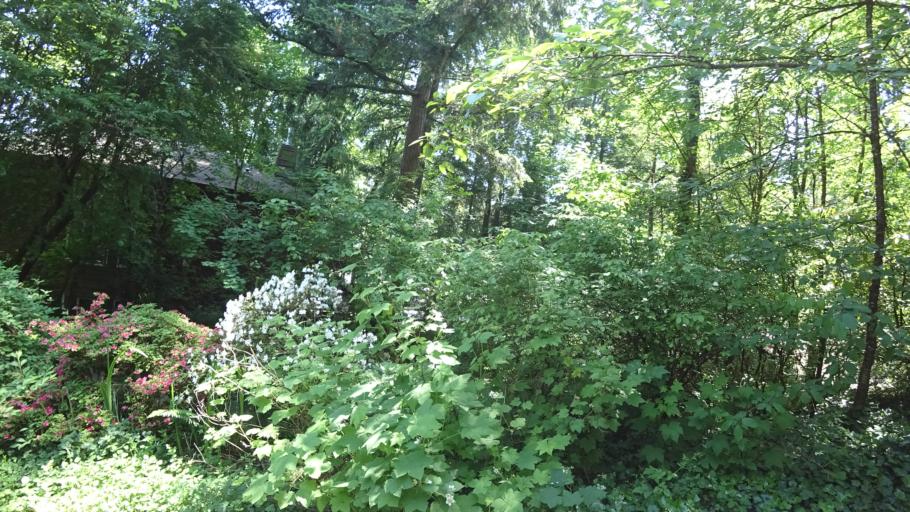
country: US
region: Oregon
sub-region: Multnomah County
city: Portland
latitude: 45.5186
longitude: -122.7145
